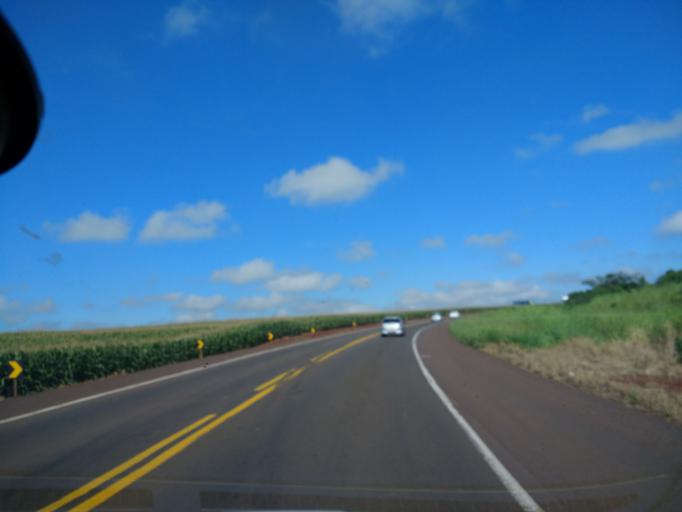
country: BR
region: Parana
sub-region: Paicandu
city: Paicandu
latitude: -23.5175
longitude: -52.1851
